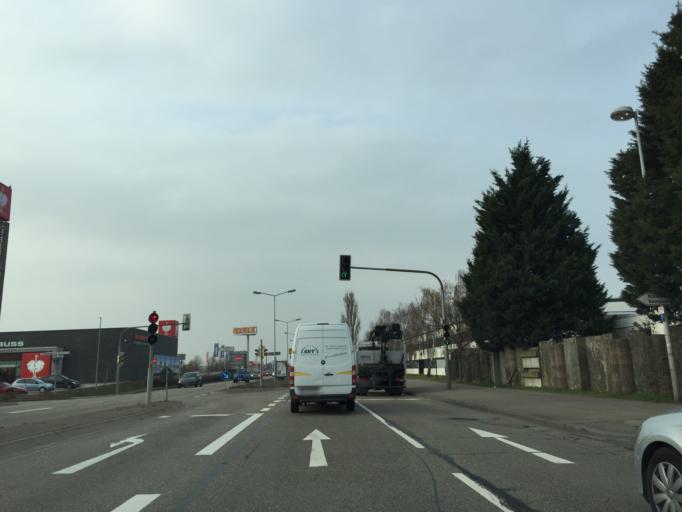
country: DE
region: Baden-Wuerttemberg
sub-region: Karlsruhe Region
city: Hockenheim
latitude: 49.3267
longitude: 8.5389
